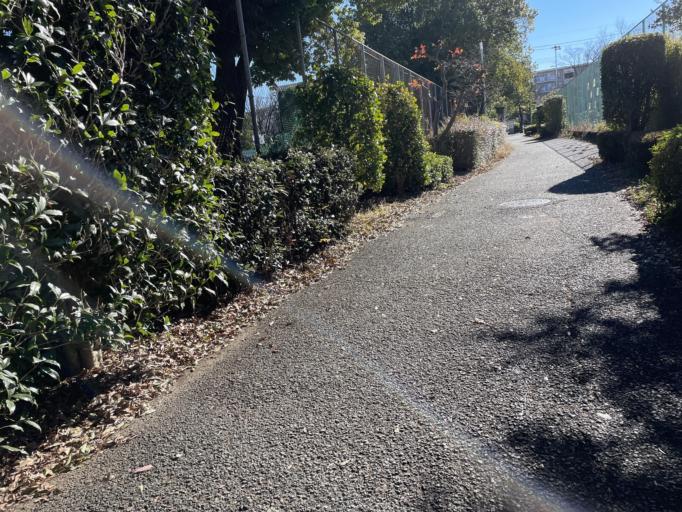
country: JP
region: Saitama
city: Sakado
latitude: 35.9248
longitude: 139.4066
